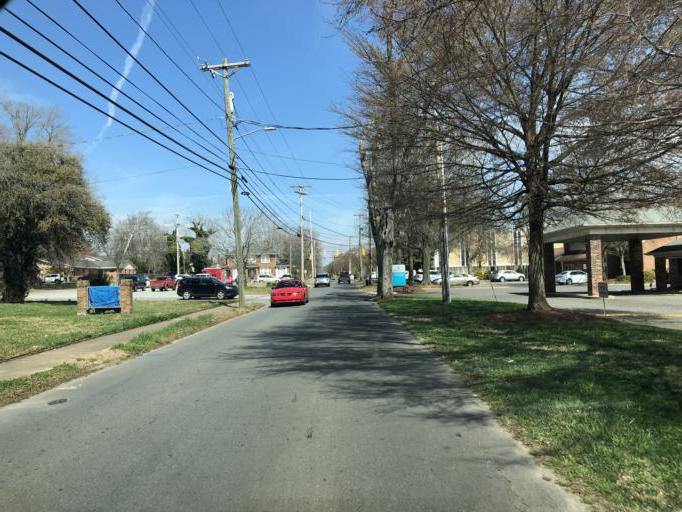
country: US
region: North Carolina
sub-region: Cleveland County
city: Shelby
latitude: 35.3003
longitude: -81.5380
